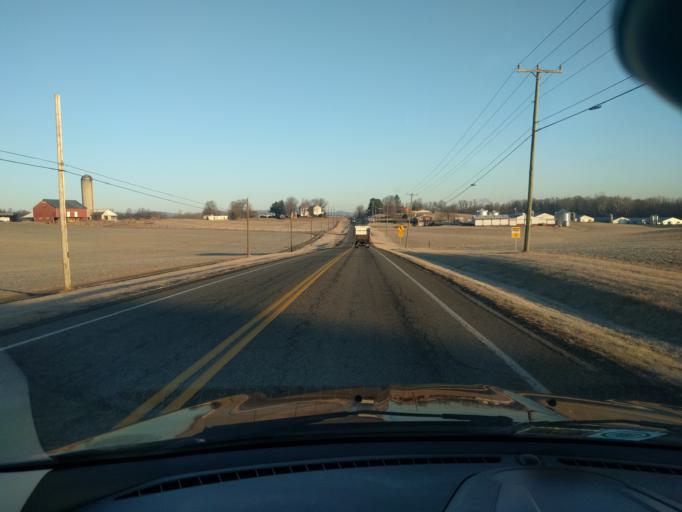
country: US
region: Virginia
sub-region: Augusta County
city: Weyers Cave
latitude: 38.3381
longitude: -78.9393
